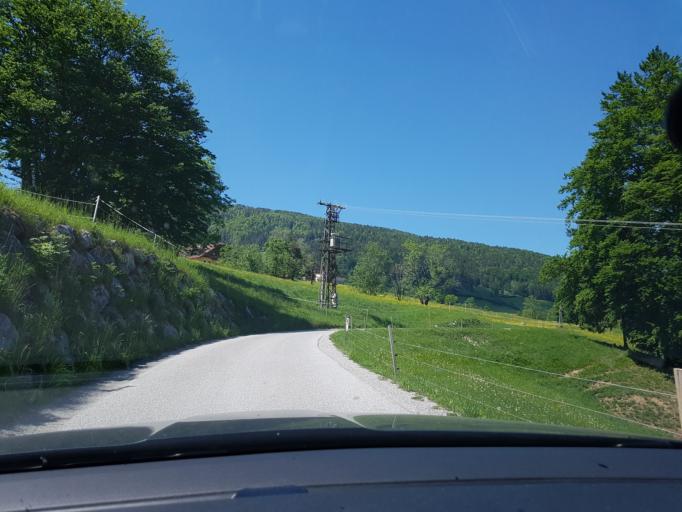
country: AT
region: Salzburg
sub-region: Politischer Bezirk Salzburg-Umgebung
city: Koppl
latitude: 47.7869
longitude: 13.1248
